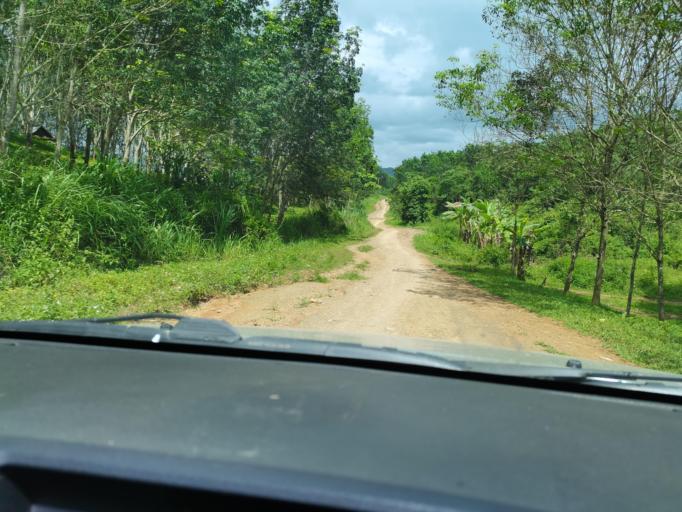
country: LA
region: Loungnamtha
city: Muang Long
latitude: 20.6851
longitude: 101.0453
